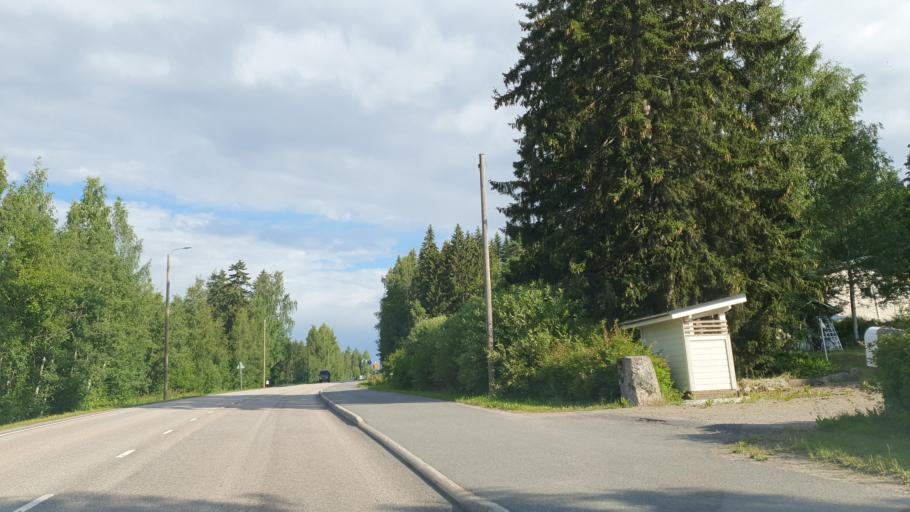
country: FI
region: Central Finland
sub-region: Jyvaeskylae
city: Saeynaetsalo
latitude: 62.1590
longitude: 25.7527
